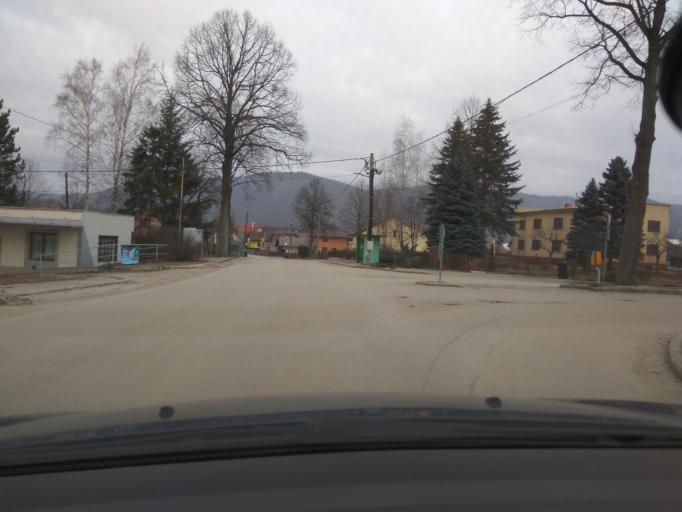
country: SK
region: Zilinsky
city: Rajec
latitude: 49.1138
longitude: 18.6781
